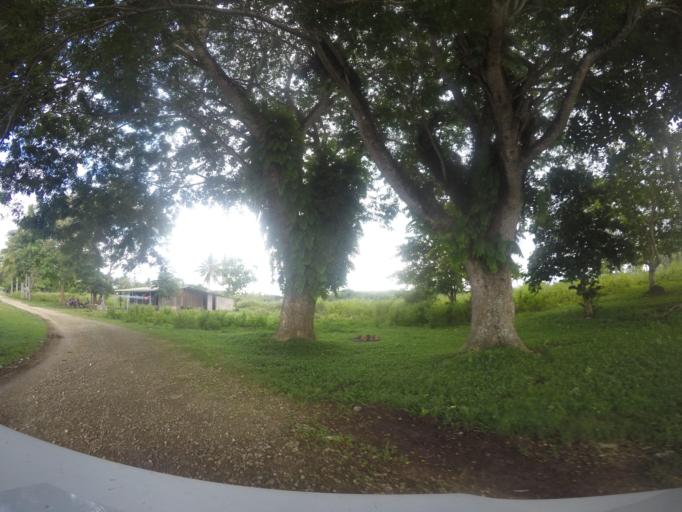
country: TL
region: Lautem
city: Lospalos
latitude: -8.5084
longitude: 126.9856
